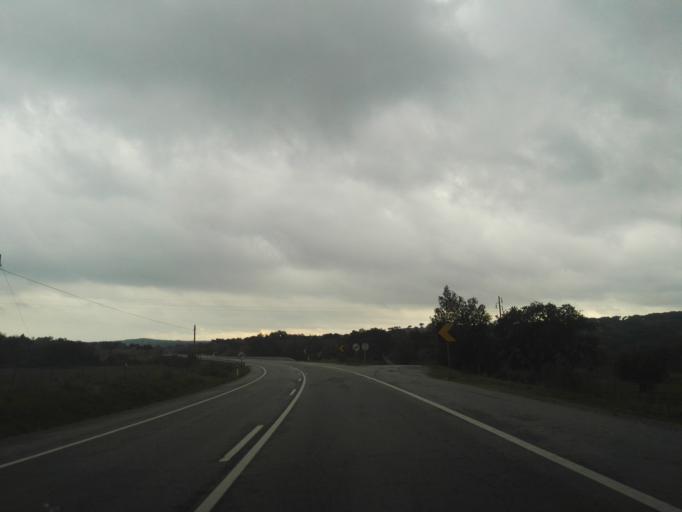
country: PT
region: Portalegre
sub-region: Portalegre
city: Urra
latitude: 39.1981
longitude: -7.3647
